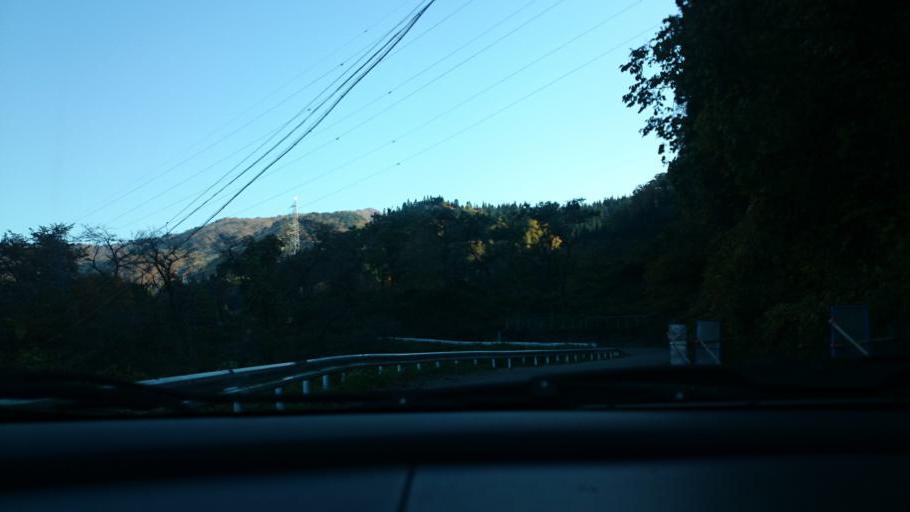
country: JP
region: Fukushima
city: Kitakata
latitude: 37.4614
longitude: 139.5946
